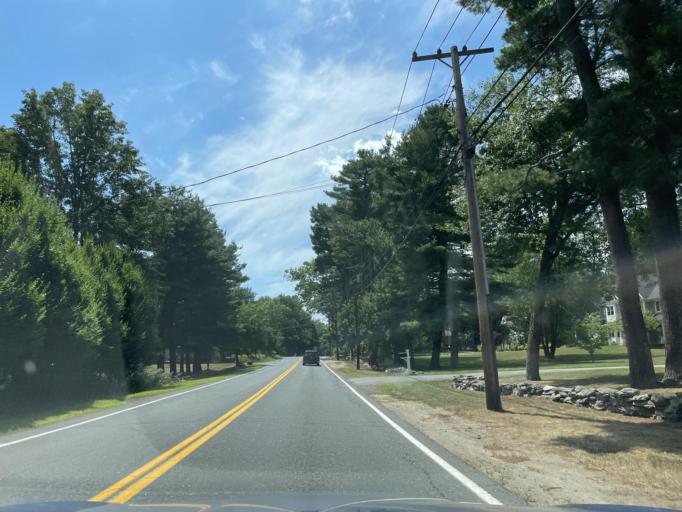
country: US
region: Massachusetts
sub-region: Middlesex County
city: Natick
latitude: 42.2599
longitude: -71.3304
